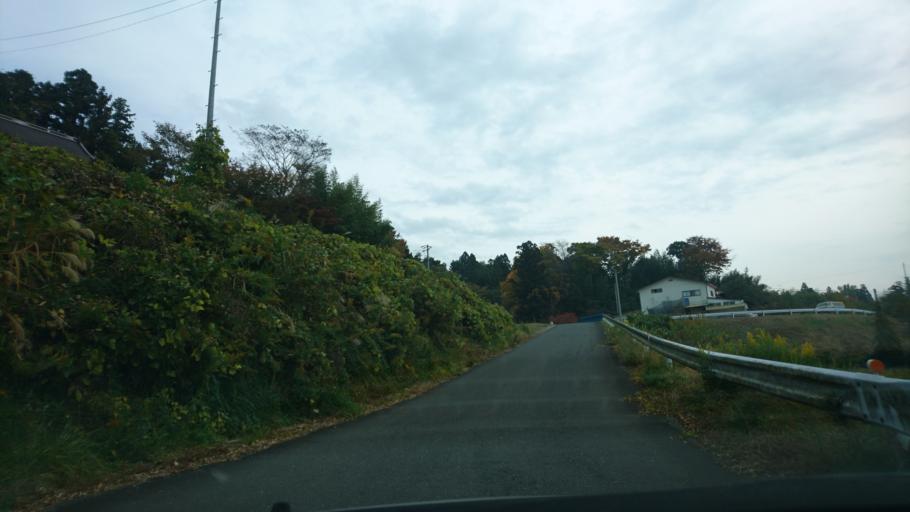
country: JP
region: Iwate
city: Ichinoseki
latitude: 38.9761
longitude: 141.1568
